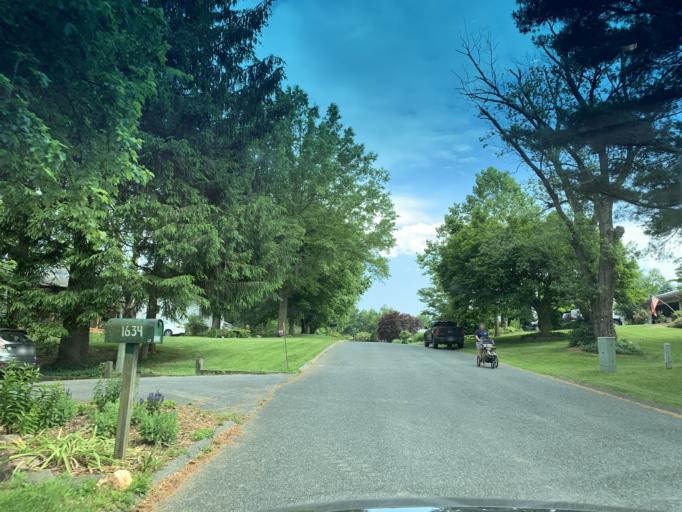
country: US
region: Maryland
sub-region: Harford County
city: Jarrettsville
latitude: 39.6056
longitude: -76.4685
